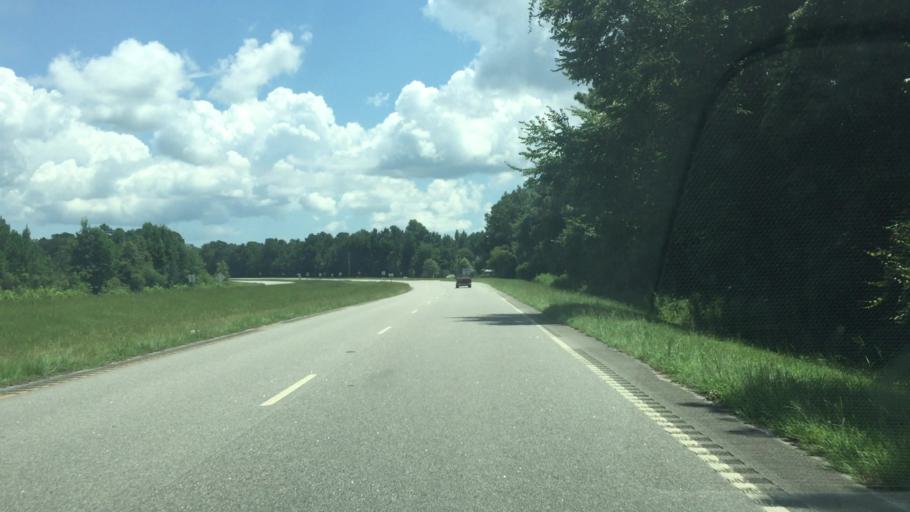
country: US
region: South Carolina
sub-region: Horry County
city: Loris
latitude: 34.0200
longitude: -78.7953
